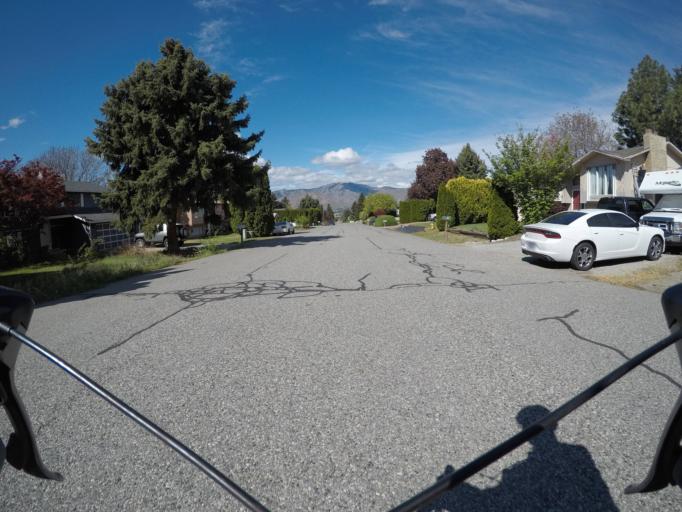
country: US
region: Washington
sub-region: Douglas County
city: East Wenatchee Bench
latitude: 47.4228
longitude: -120.2734
